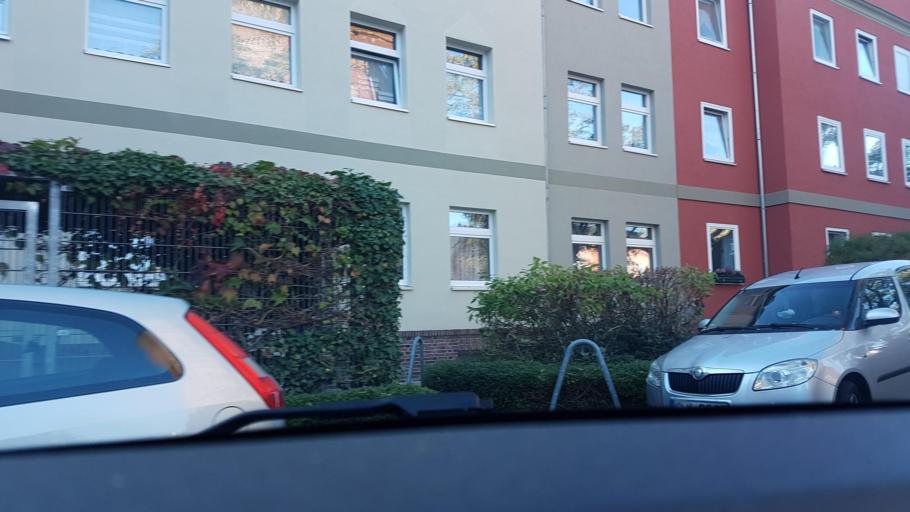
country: DE
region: Saxony-Anhalt
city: Bernburg
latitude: 51.7877
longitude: 11.7345
